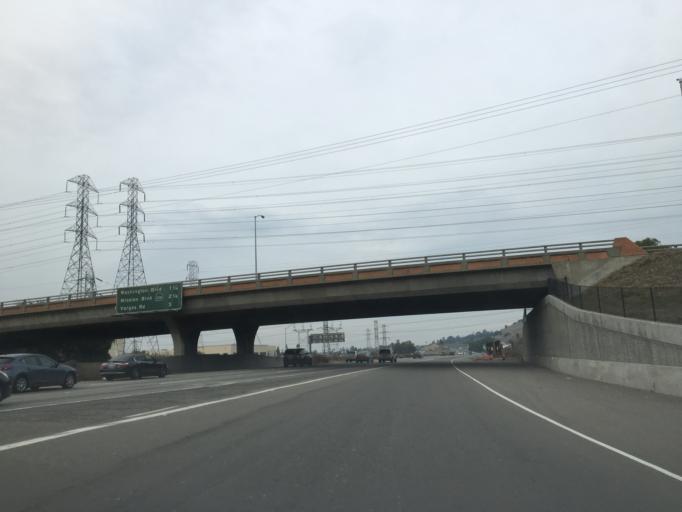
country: US
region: California
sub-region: Alameda County
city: Fremont
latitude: 37.5142
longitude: -121.9390
